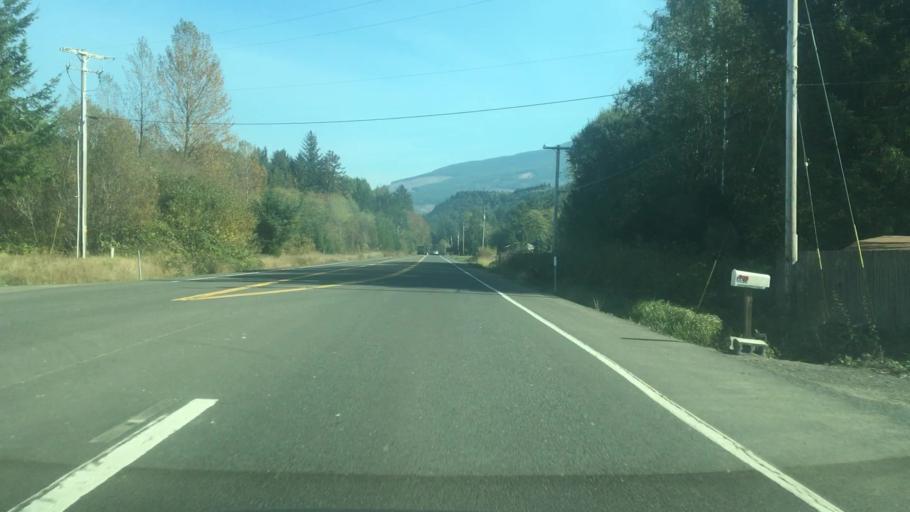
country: US
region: Oregon
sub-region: Lincoln County
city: Rose Lodge
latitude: 45.0213
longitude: -123.8581
